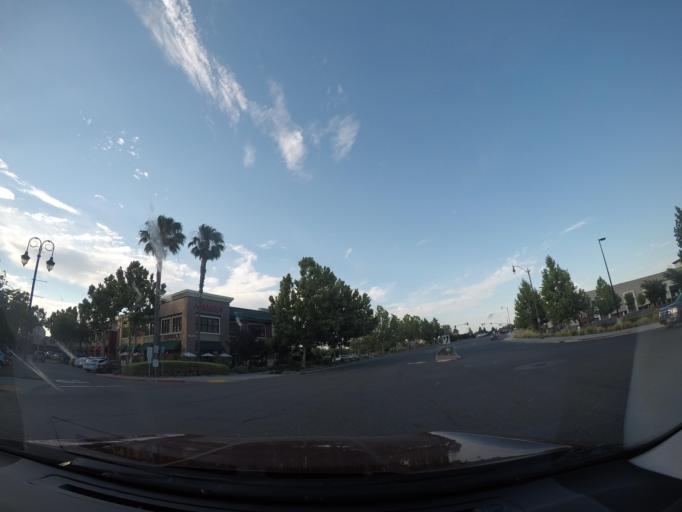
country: US
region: California
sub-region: Solano County
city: Vacaville
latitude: 38.3694
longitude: -121.9602
